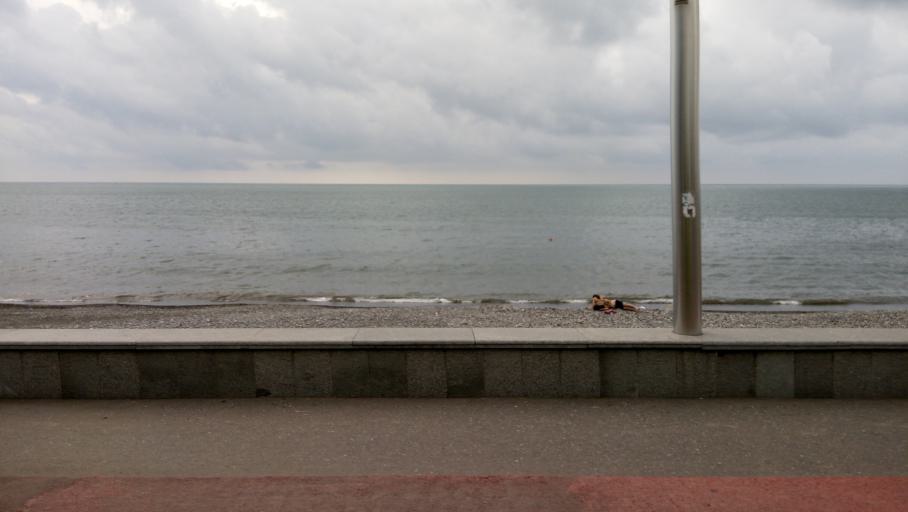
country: GE
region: Ajaria
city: Makhinjauri
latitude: 41.6574
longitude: 41.6757
